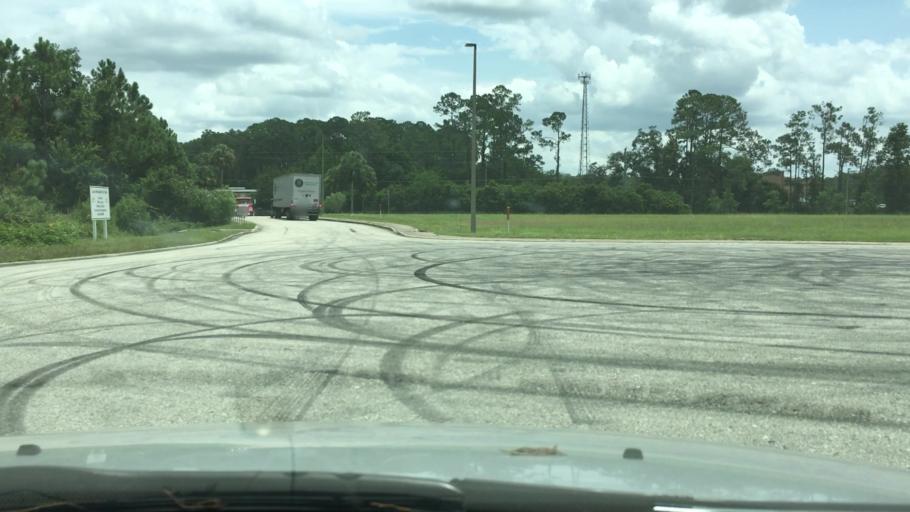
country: US
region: Florida
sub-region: Volusia County
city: Lake Helen
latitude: 29.0220
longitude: -81.2257
